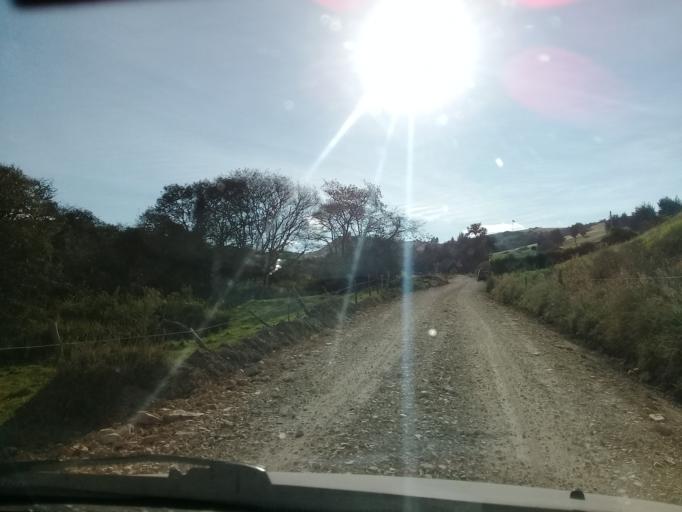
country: CO
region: Cundinamarca
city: Lenguazaque
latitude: 5.2682
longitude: -73.6599
